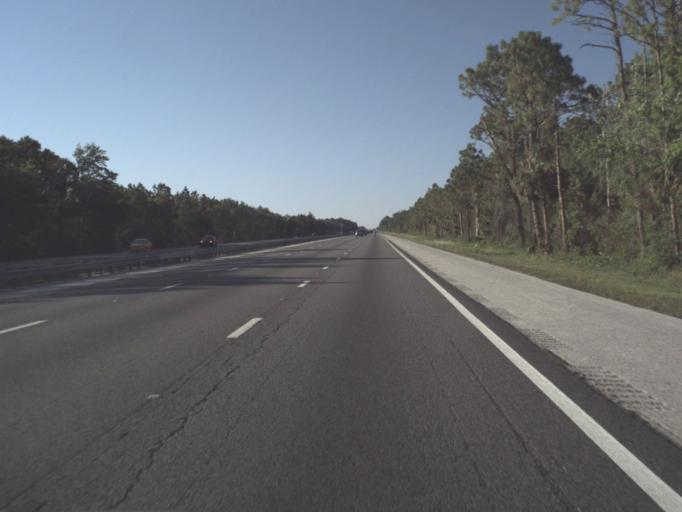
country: US
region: Florida
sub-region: Flagler County
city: Flagler Beach
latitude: 29.4497
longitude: -81.1736
